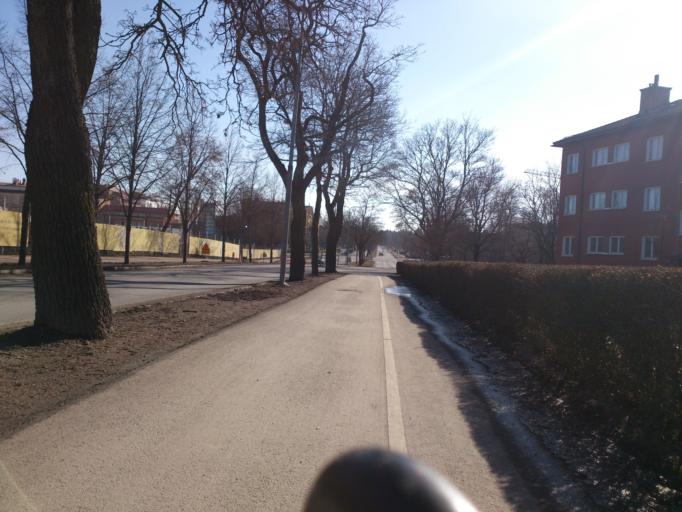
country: SE
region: Uppsala
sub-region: Uppsala Kommun
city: Uppsala
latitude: 59.8479
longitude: 17.6370
